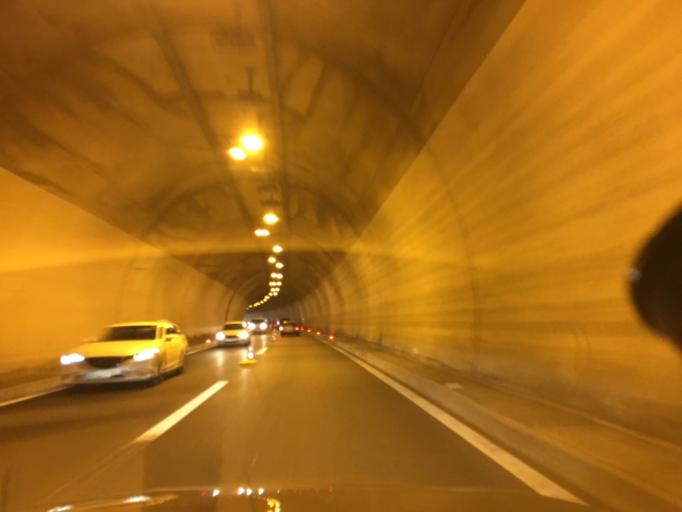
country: HR
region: Licko-Senjska
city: Otocac
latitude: 44.8706
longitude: 15.2077
